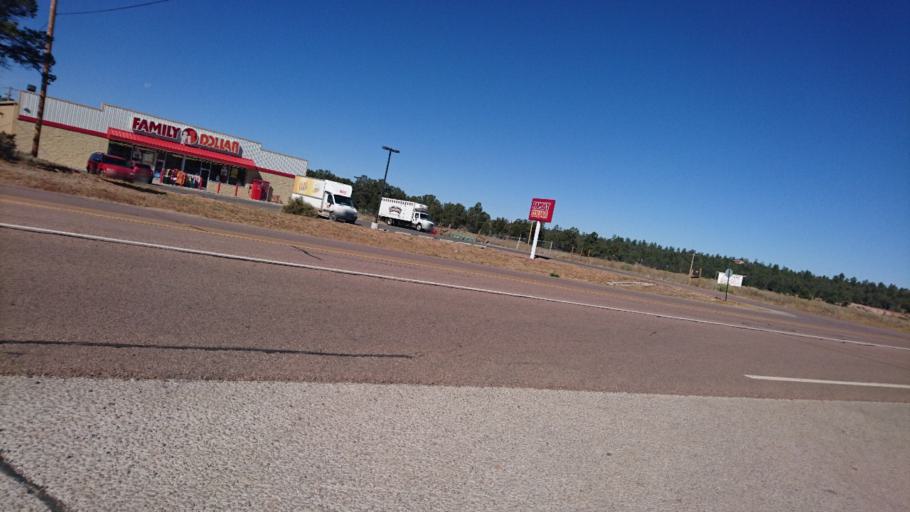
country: US
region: New Mexico
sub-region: McKinley County
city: Black Rock
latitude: 35.2351
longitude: -108.7646
